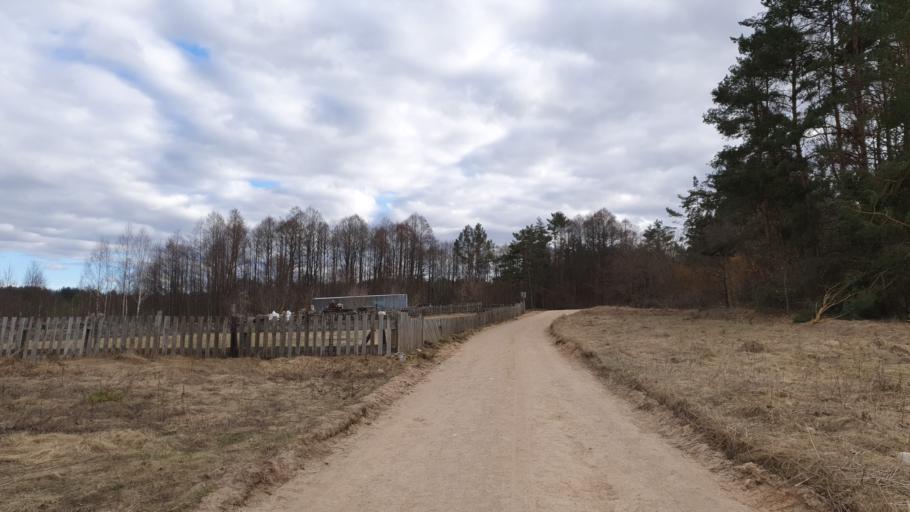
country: LT
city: Grigiskes
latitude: 54.7338
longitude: 25.0274
